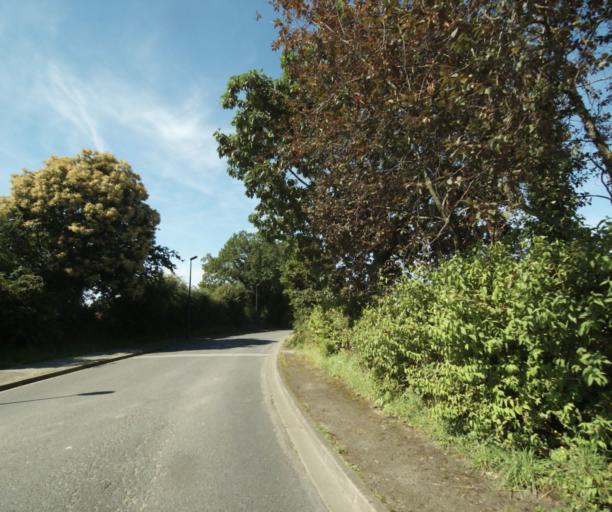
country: FR
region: Pays de la Loire
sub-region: Departement de la Mayenne
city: Laval
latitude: 48.0575
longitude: -0.7984
